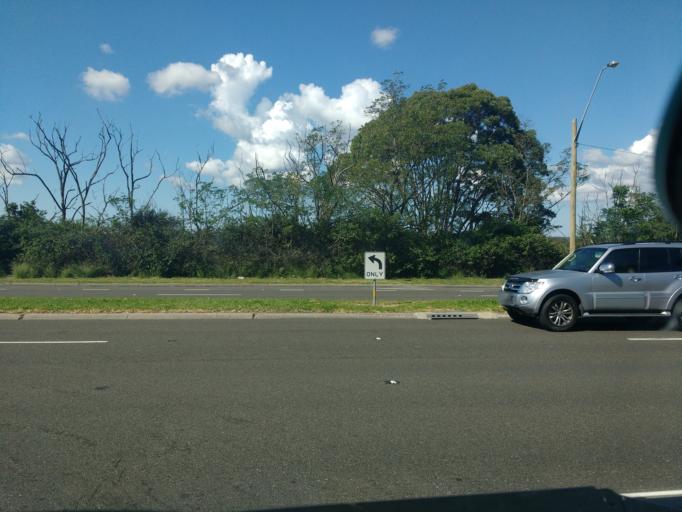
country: AU
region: New South Wales
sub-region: Hornsby Shire
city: Berowra
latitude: -33.6267
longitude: 151.1483
